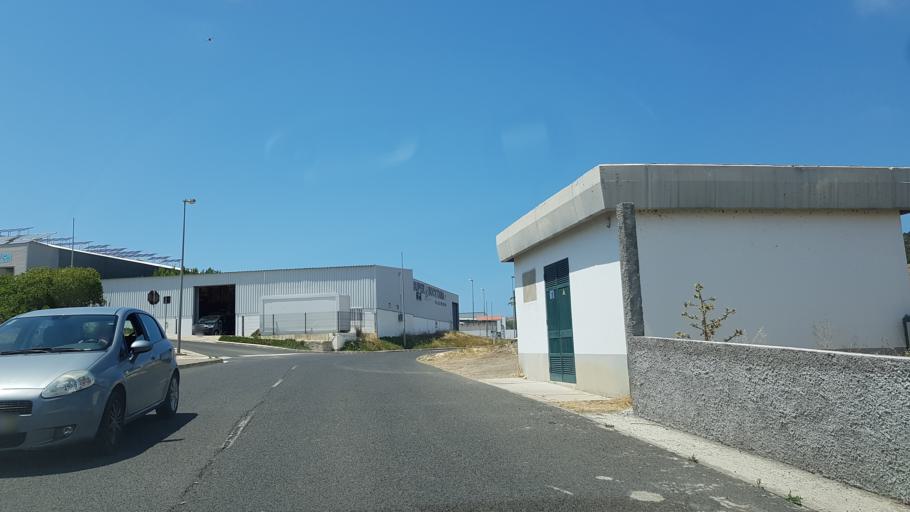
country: PT
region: Madeira
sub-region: Porto Santo
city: Vila de Porto Santo
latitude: 33.0689
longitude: -16.3422
